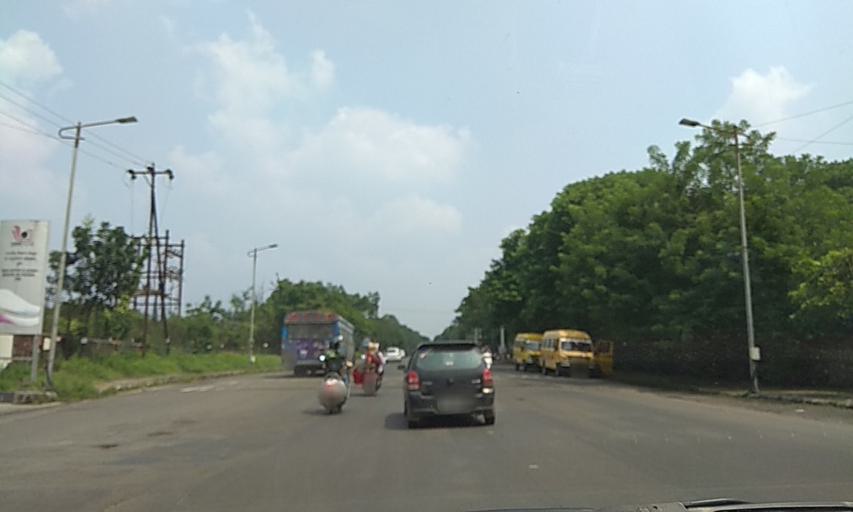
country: IN
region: Maharashtra
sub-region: Pune Division
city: Shivaji Nagar
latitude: 18.5389
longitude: 73.8085
